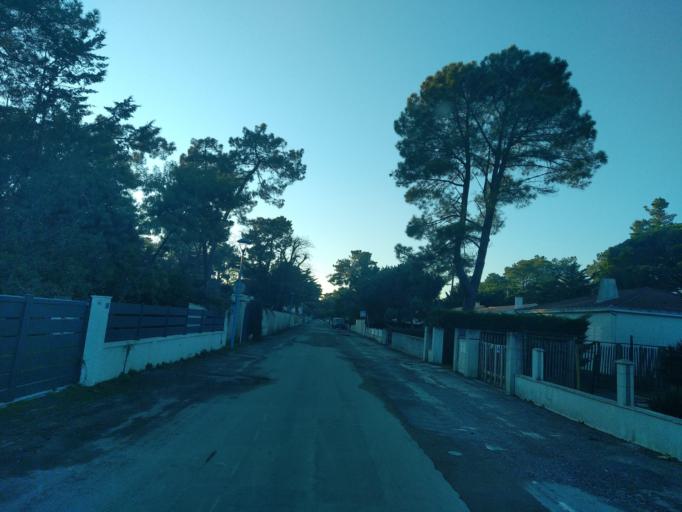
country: FR
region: Pays de la Loire
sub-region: Departement de la Vendee
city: Longeville-sur-Mer
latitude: 46.3883
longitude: -1.4783
